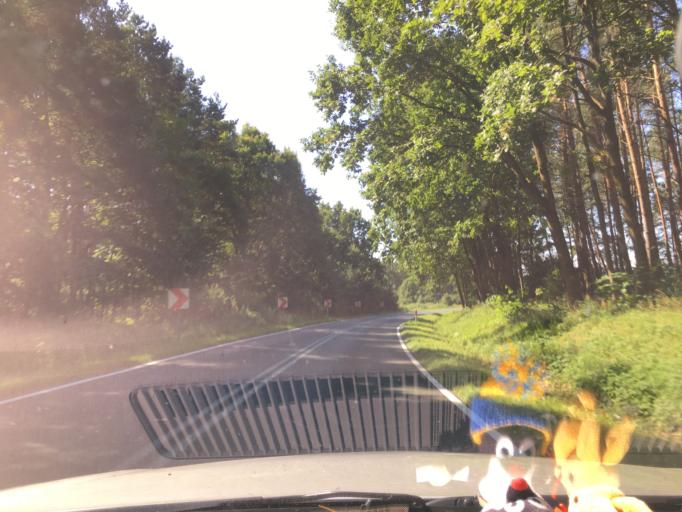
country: PL
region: West Pomeranian Voivodeship
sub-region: Powiat kamienski
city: Wolin
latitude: 53.9755
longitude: 14.6288
